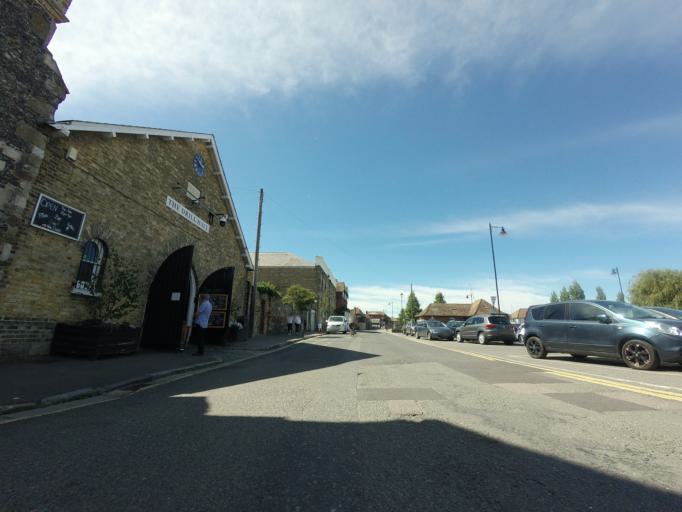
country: GB
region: England
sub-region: Kent
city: Sandwich
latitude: 51.2752
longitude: 1.3434
